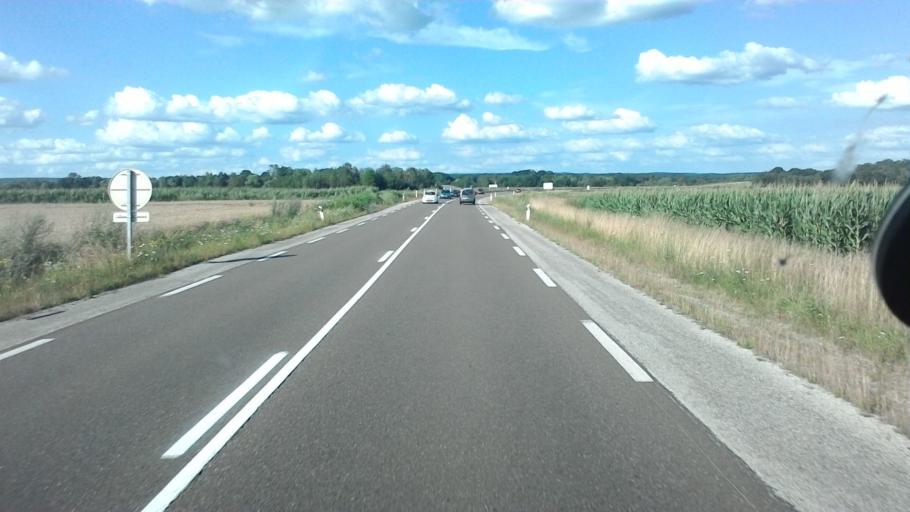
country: FR
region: Franche-Comte
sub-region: Departement de la Haute-Saone
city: Saint-Sauveur
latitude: 47.7828
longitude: 6.3758
